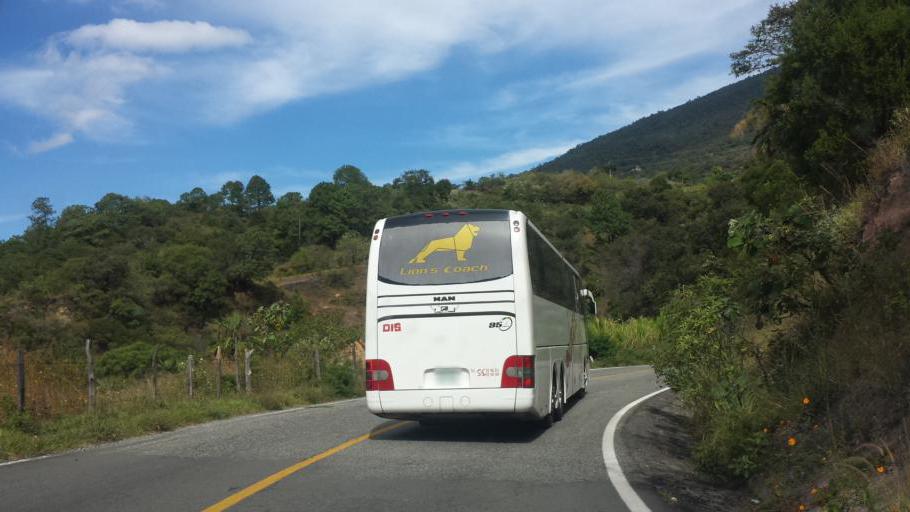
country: MX
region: Oaxaca
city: San Francisco Sola
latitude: 16.4569
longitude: -97.0271
